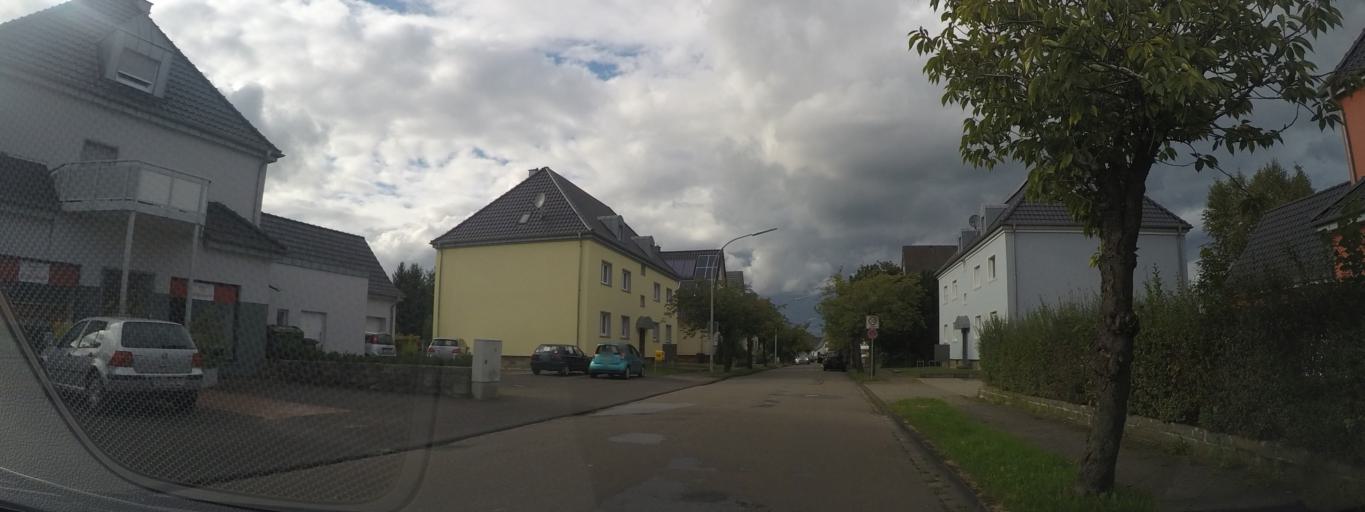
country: DE
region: North Rhine-Westphalia
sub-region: Regierungsbezirk Arnsberg
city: Lippstadt
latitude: 51.6821
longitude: 8.3329
